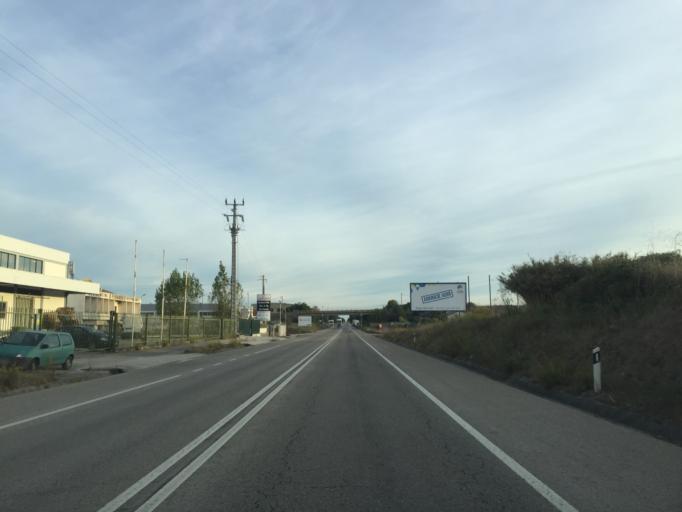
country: PT
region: Leiria
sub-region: Alcobaca
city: Benedita
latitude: 39.4306
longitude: -8.9582
